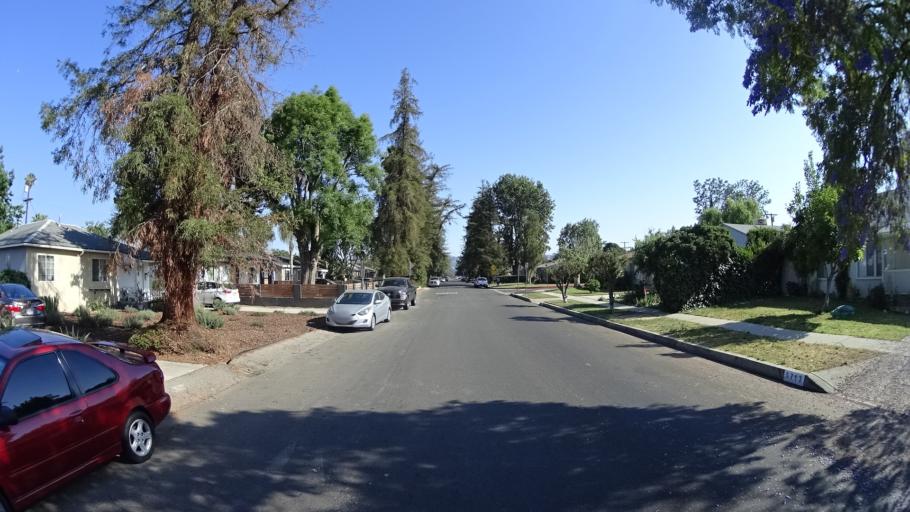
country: US
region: California
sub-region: Los Angeles County
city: Van Nuys
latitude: 34.1744
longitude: -118.4531
